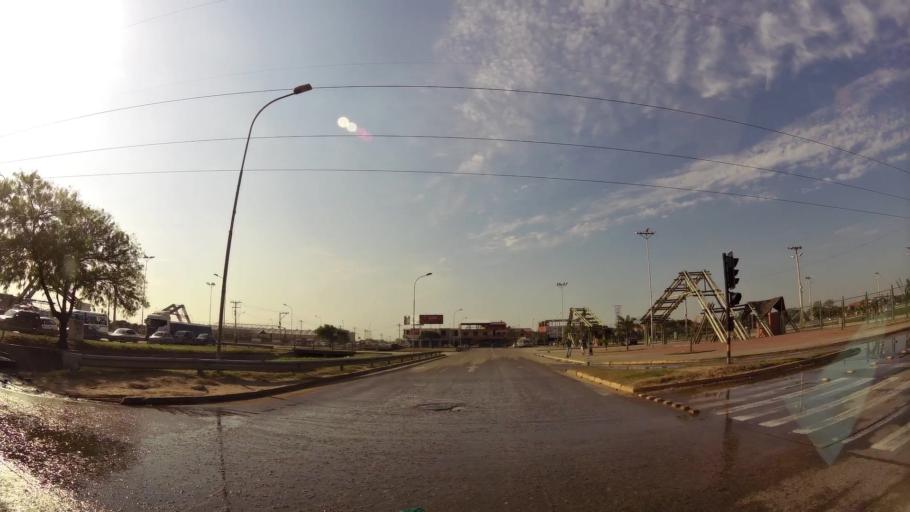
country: BO
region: Santa Cruz
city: Santa Cruz de la Sierra
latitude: -17.7422
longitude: -63.1464
